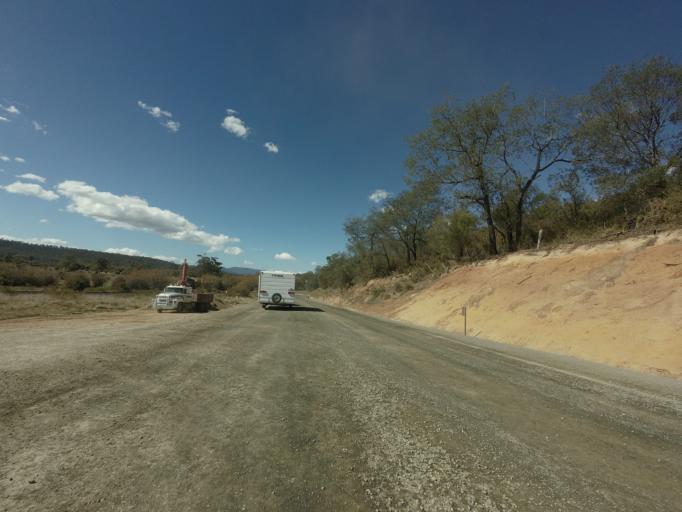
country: AU
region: Tasmania
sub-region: Break O'Day
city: St Helens
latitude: -41.6512
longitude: 147.9283
